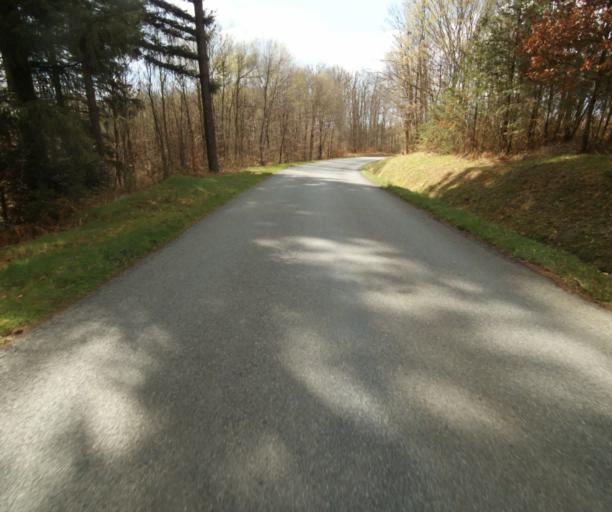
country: FR
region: Limousin
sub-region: Departement de la Correze
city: Argentat
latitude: 45.2332
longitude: 1.9354
